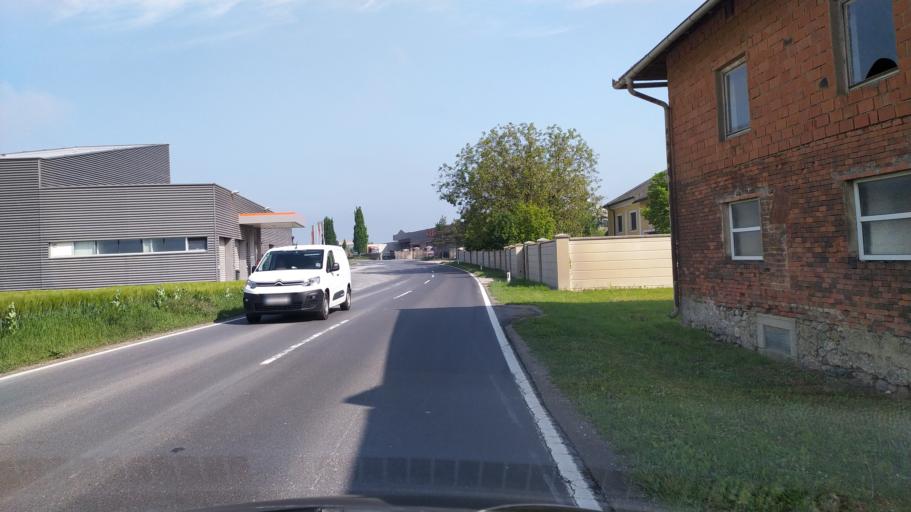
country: AT
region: Lower Austria
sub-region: Politischer Bezirk Amstetten
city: Ennsdorf
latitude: 48.2145
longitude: 14.5415
